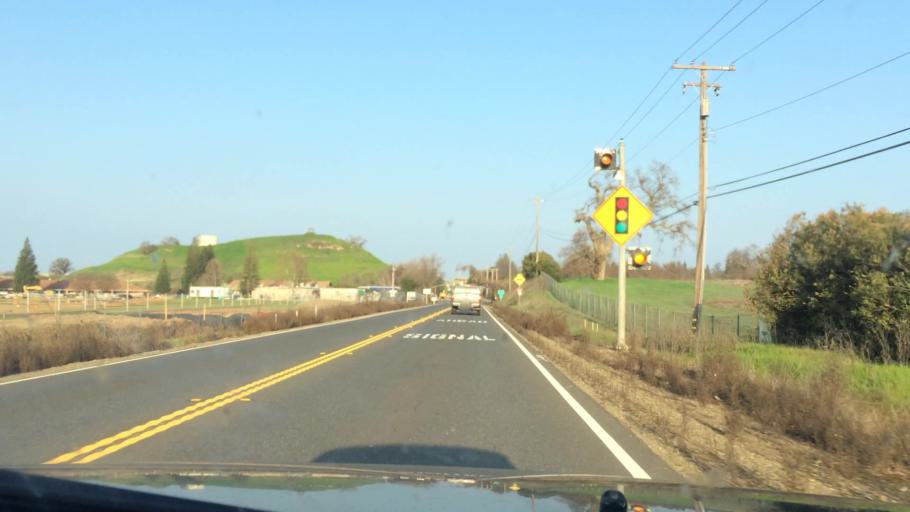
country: US
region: California
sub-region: Sacramento County
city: Rancho Murieta
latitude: 38.4946
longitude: -121.0952
